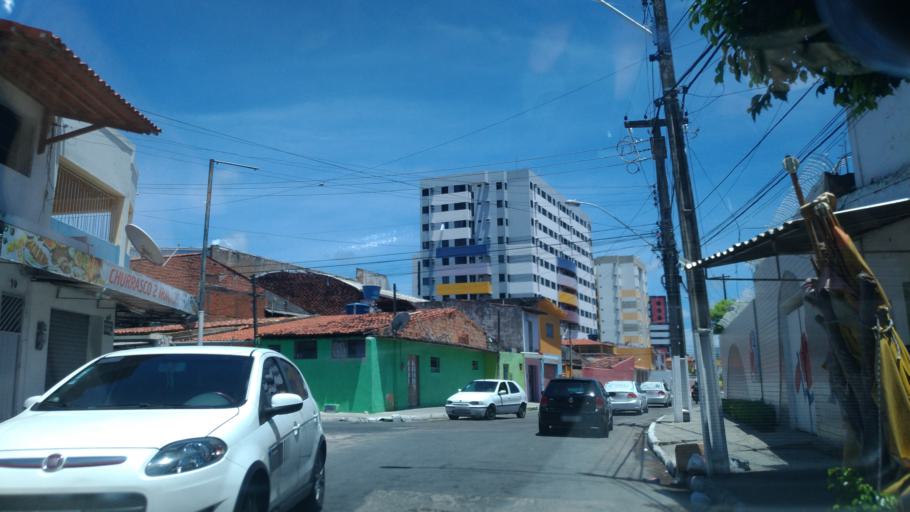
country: BR
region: Alagoas
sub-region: Maceio
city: Maceio
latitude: -9.6623
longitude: -35.7117
